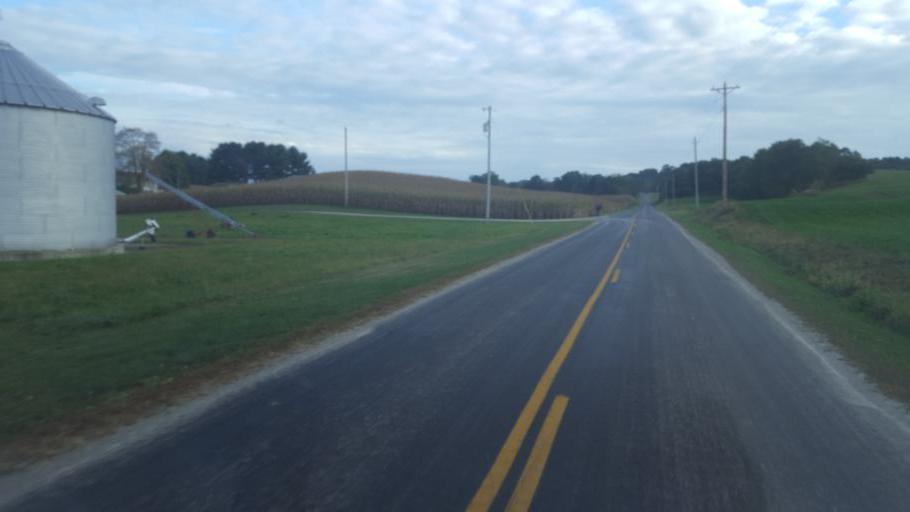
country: US
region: Ohio
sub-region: Ashland County
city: Loudonville
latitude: 40.7095
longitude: -82.1694
